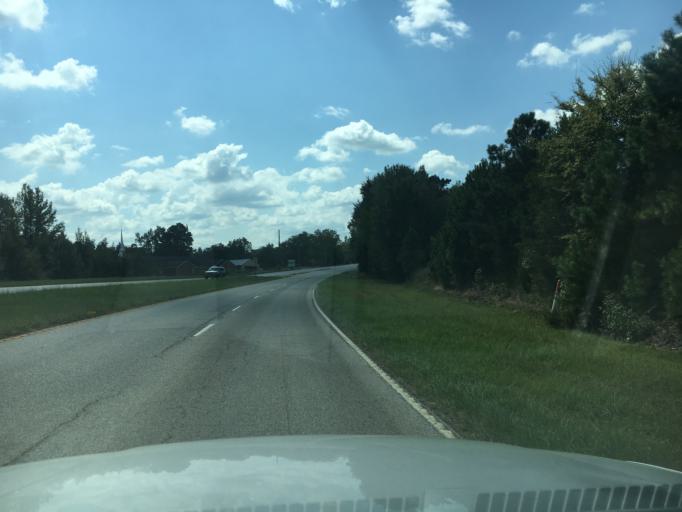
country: US
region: South Carolina
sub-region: Greenwood County
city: Ware Shoals
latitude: 34.2985
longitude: -82.2229
